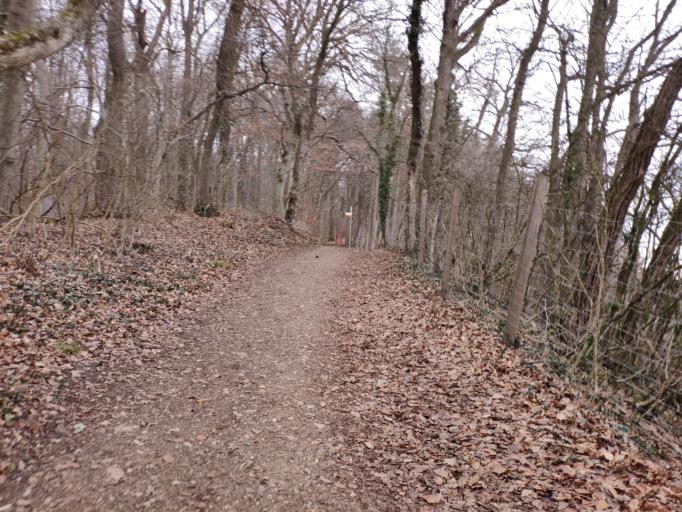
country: CH
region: Basel-City
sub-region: Basel-Stadt
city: Bettingen
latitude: 47.5590
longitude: 7.6487
